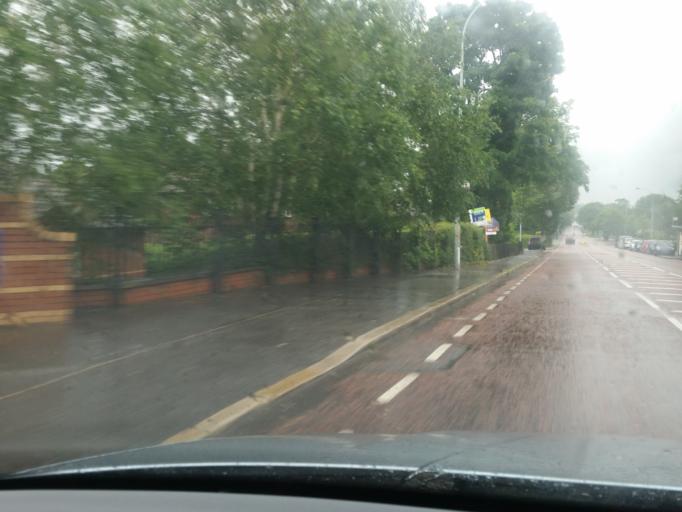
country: GB
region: Northern Ireland
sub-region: Castlereagh District
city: Castlereagh
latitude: 54.6068
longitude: -5.8706
